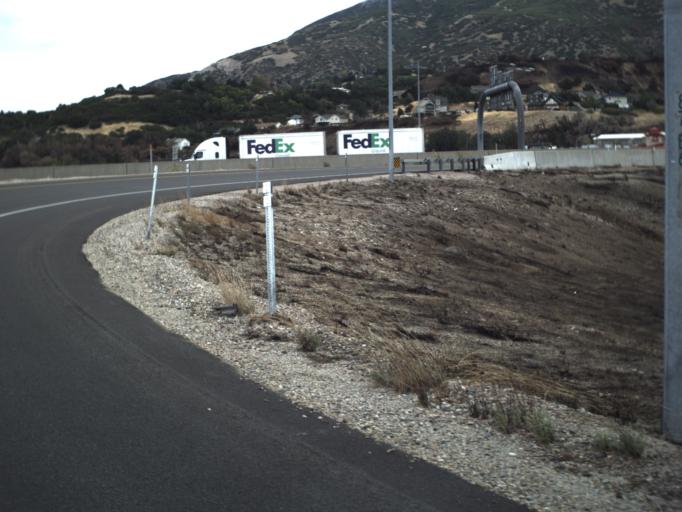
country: US
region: Utah
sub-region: Weber County
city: Uintah
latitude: 41.1362
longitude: -111.9153
